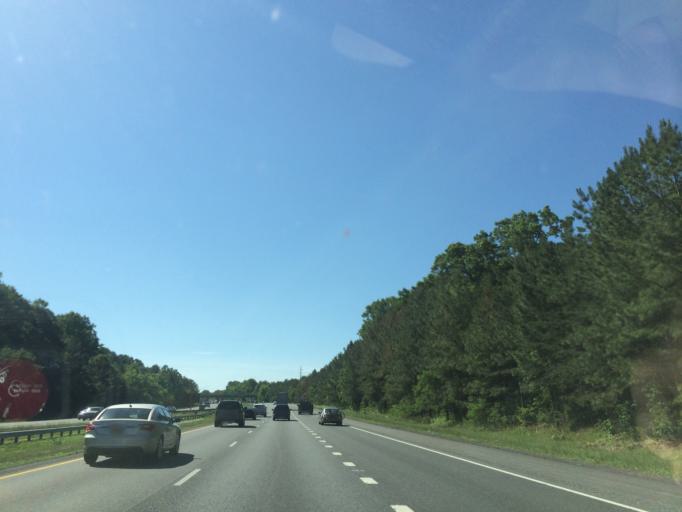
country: US
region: Maryland
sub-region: Anne Arundel County
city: Crownsville
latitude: 39.0517
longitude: -76.6269
